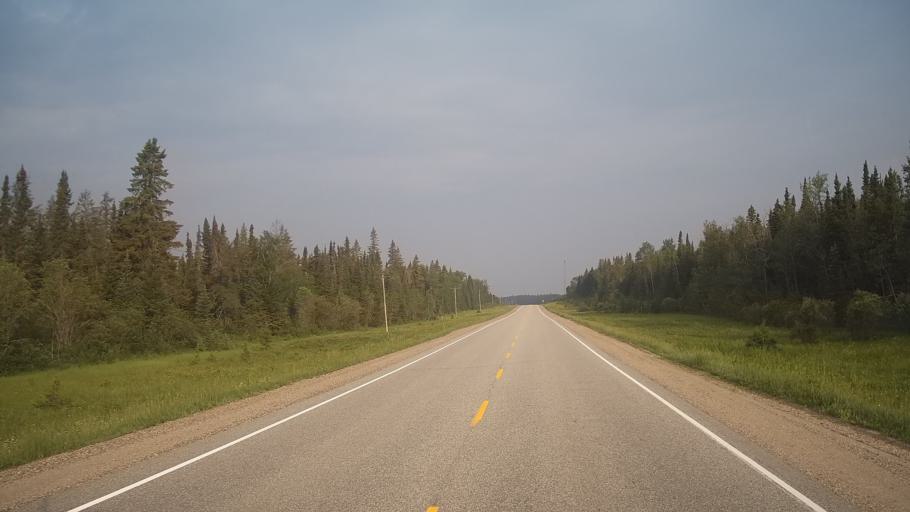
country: CA
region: Ontario
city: Hearst
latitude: 49.7366
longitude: -83.9443
